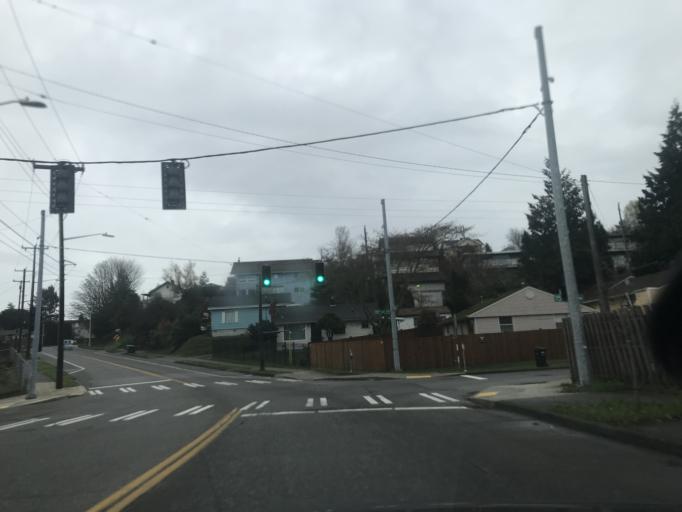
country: US
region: Washington
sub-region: King County
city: White Center
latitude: 47.5337
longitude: -122.3543
